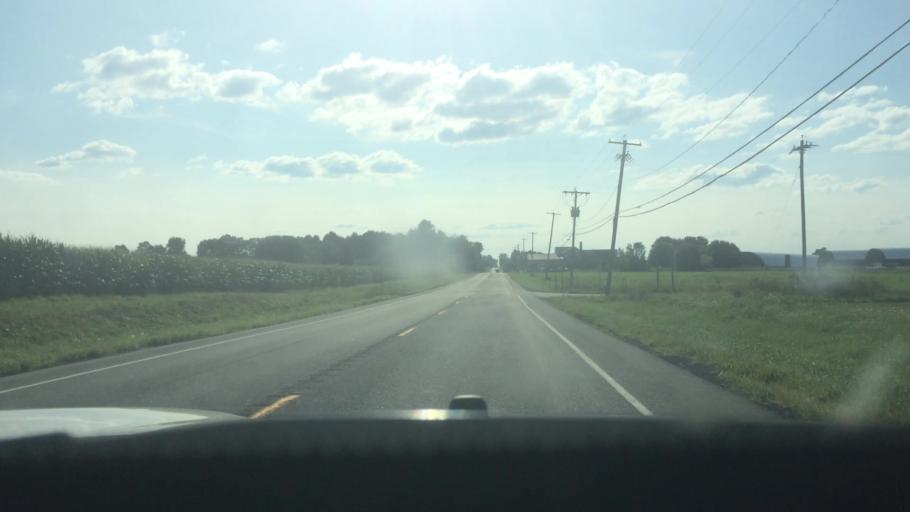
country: US
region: New York
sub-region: St. Lawrence County
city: Hannawa Falls
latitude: 44.6927
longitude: -74.6738
